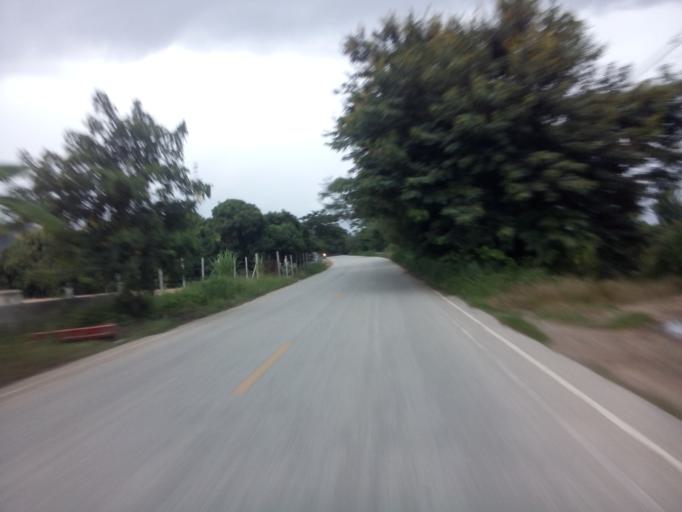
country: TH
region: Chiang Mai
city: Mae Wang
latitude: 18.6118
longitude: 98.7804
